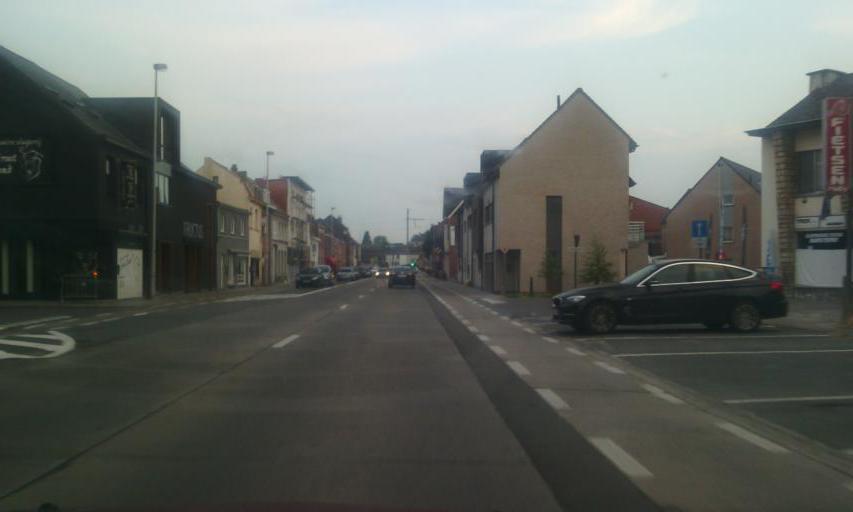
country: BE
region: Flanders
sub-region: Provincie Oost-Vlaanderen
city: Dendermonde
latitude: 51.0433
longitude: 4.1044
